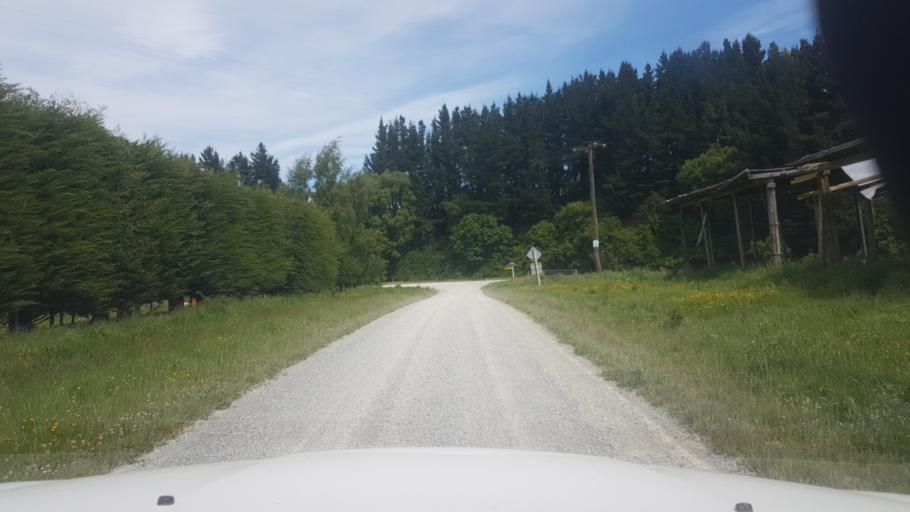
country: NZ
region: Canterbury
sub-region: Timaru District
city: Pleasant Point
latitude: -44.1875
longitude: 171.0543
